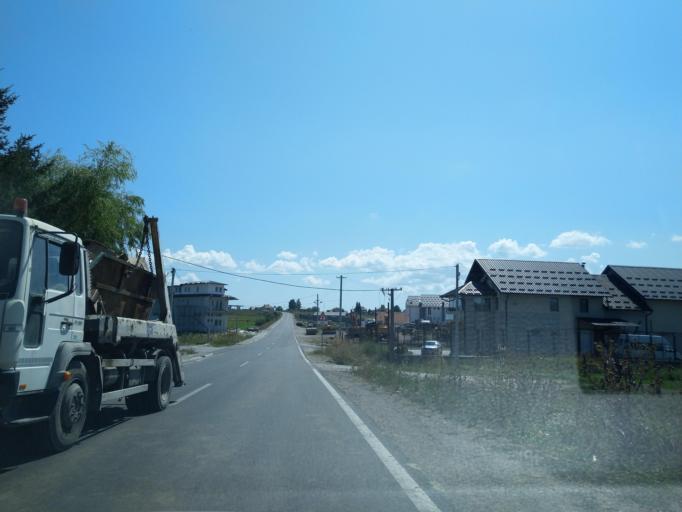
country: RS
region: Central Serbia
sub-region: Zlatiborski Okrug
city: Sjenica
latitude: 43.2781
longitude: 19.9821
